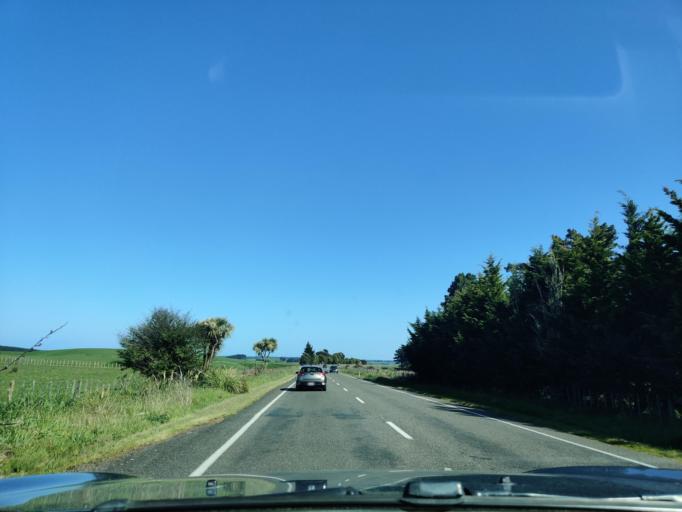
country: NZ
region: Manawatu-Wanganui
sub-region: Rangitikei District
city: Bulls
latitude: -40.0785
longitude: 175.2405
